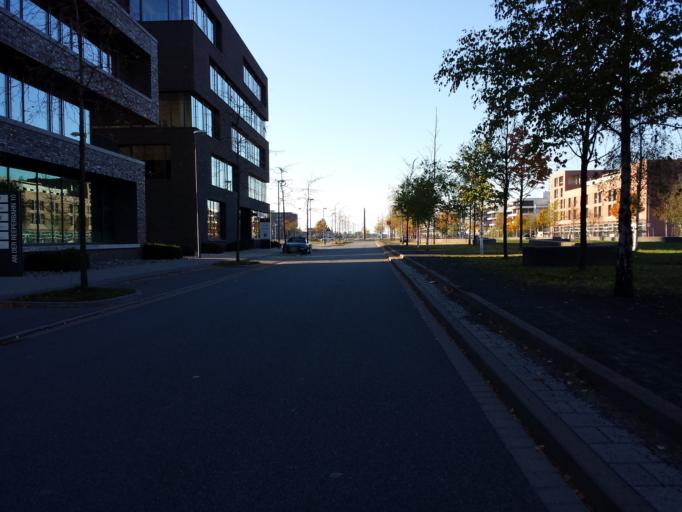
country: DE
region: Bremen
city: Bremen
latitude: 53.0848
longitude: 8.7835
